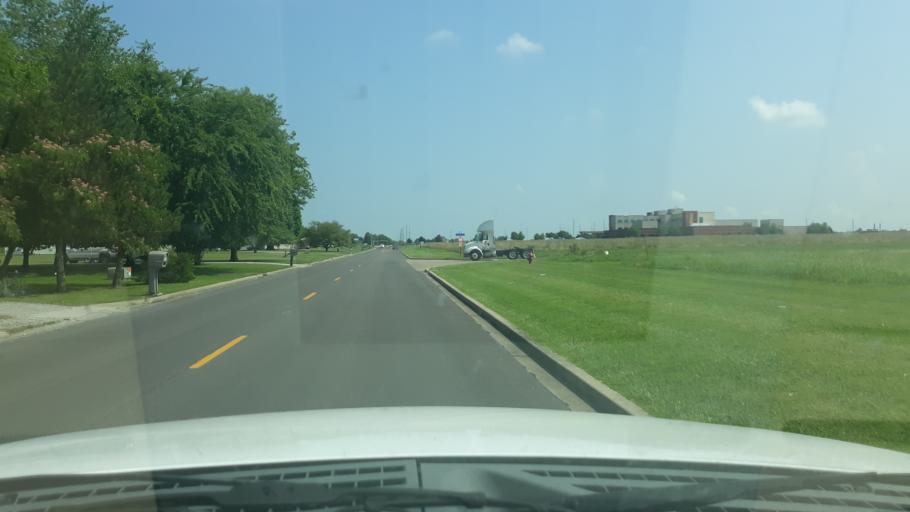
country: US
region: Illinois
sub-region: Williamson County
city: Energy
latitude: 37.7388
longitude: -88.9932
